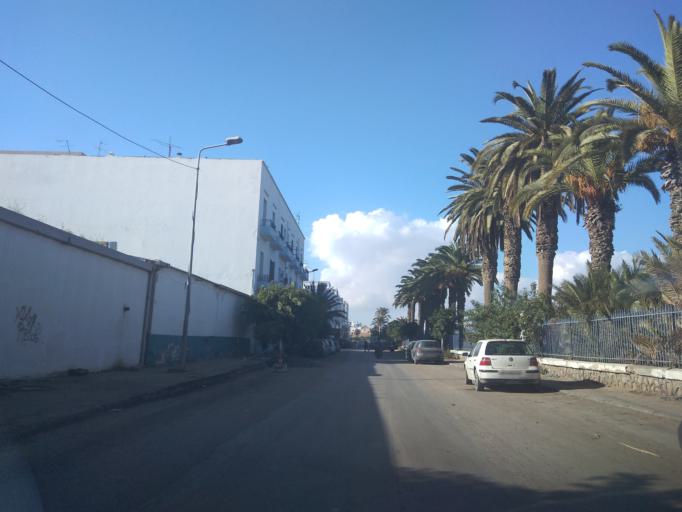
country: TN
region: Safaqis
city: Sfax
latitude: 34.7327
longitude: 10.7684
